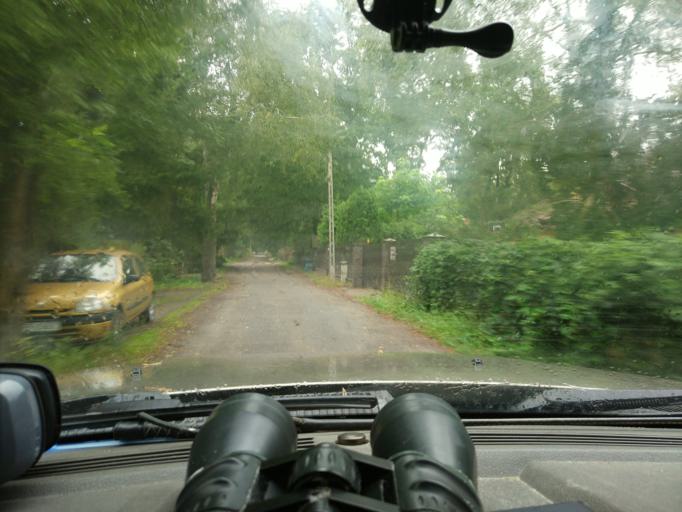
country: PL
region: Masovian Voivodeship
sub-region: Powiat grodziski
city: Podkowa Lesna
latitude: 52.1284
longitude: 20.7346
